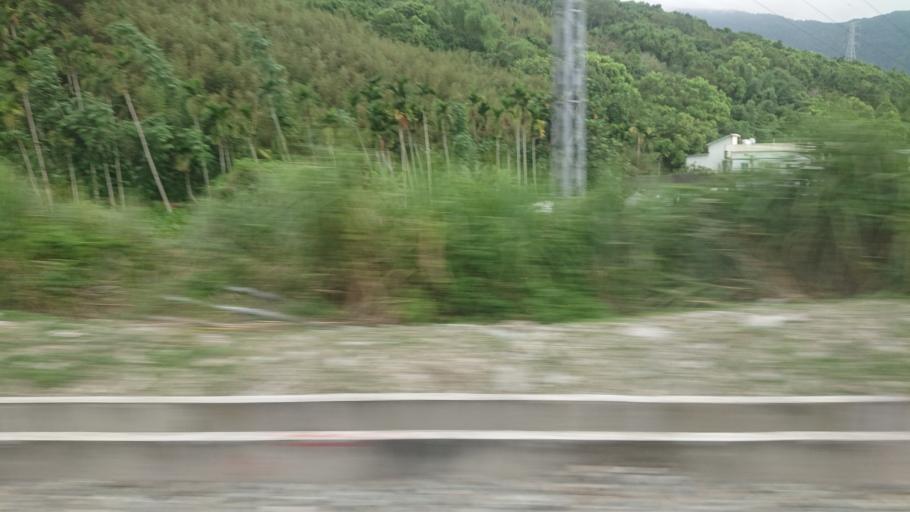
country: TW
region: Taiwan
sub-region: Hualien
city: Hualian
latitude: 23.7311
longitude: 121.4383
